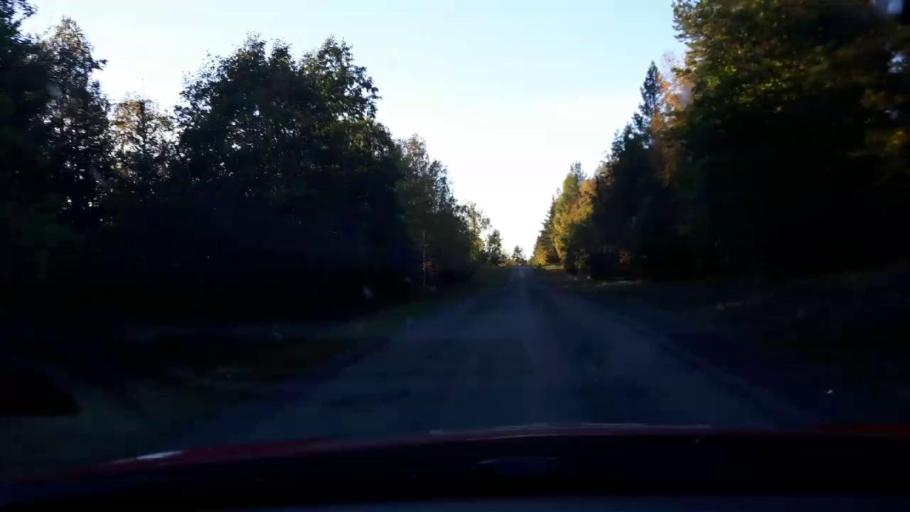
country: SE
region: Jaemtland
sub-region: Krokoms Kommun
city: Krokom
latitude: 63.4157
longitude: 14.6157
